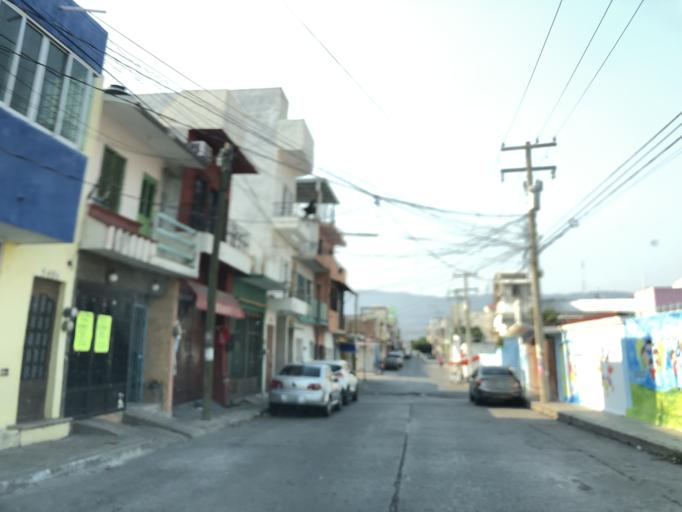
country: MX
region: Chiapas
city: Tuxtla Gutierrez
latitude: 16.7503
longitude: -93.1220
